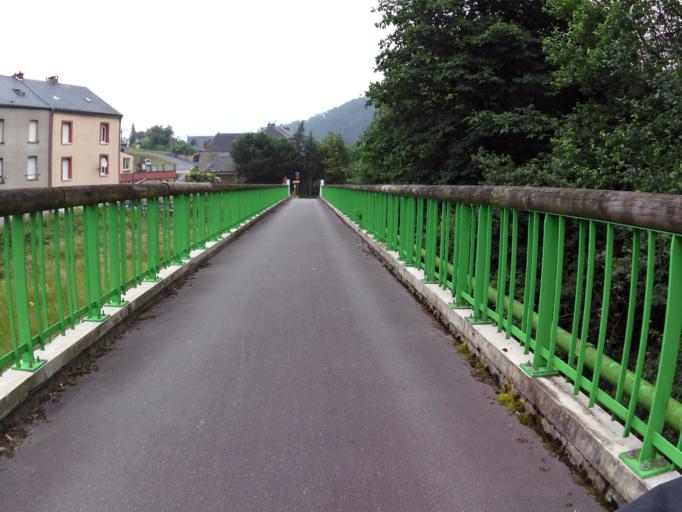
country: FR
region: Champagne-Ardenne
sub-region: Departement des Ardennes
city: Fumay
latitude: 49.9787
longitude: 4.6862
